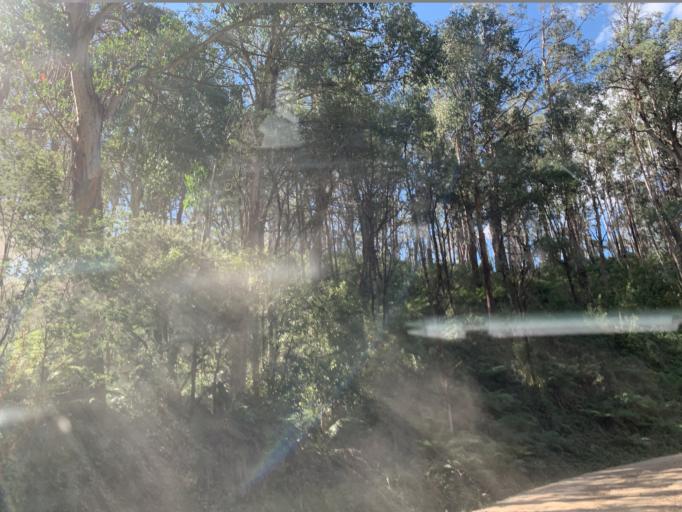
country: AU
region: Victoria
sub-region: Mansfield
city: Mansfield
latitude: -37.1027
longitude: 146.4974
